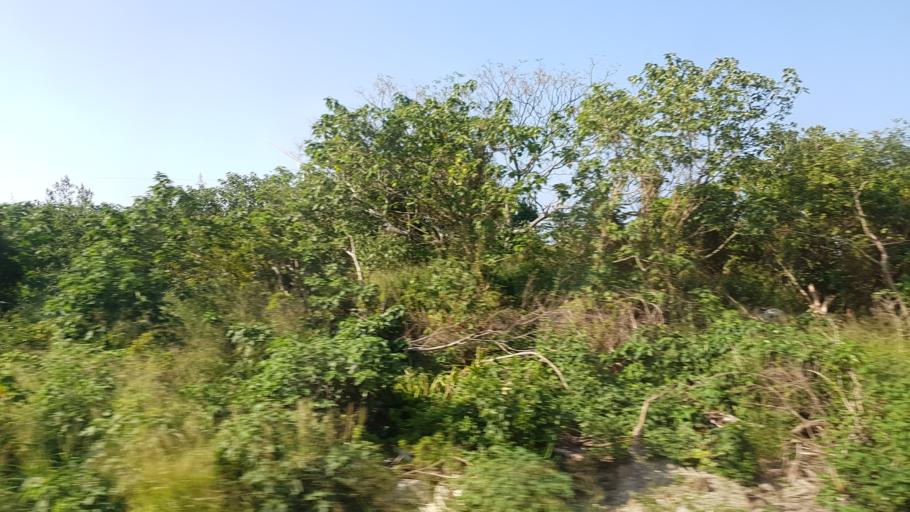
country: TW
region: Taiwan
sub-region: Hsinchu
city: Hsinchu
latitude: 24.7370
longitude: 120.8907
